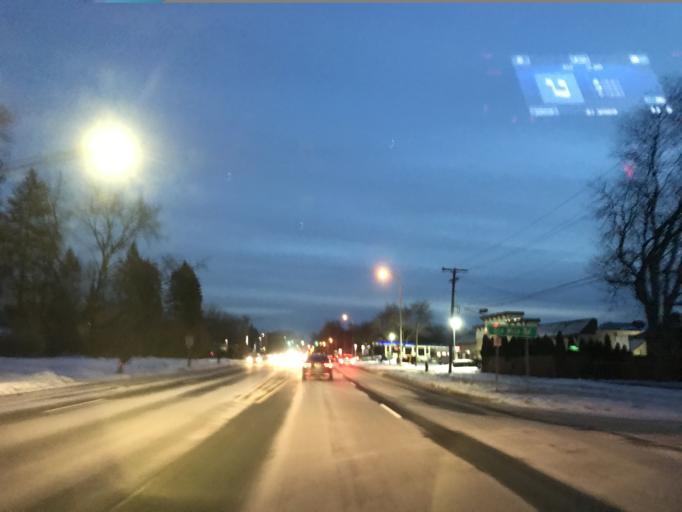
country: US
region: Michigan
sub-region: Wayne County
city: Redford
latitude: 42.4154
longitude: -83.3157
